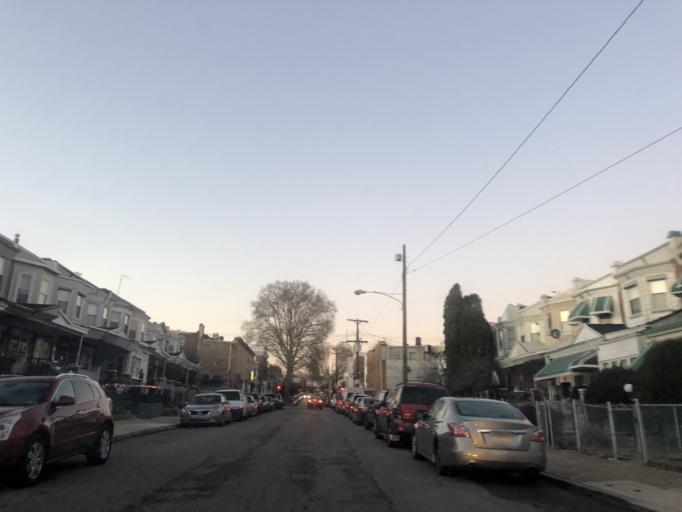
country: US
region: Pennsylvania
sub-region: Delaware County
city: Millbourne
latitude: 39.9746
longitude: -75.2434
